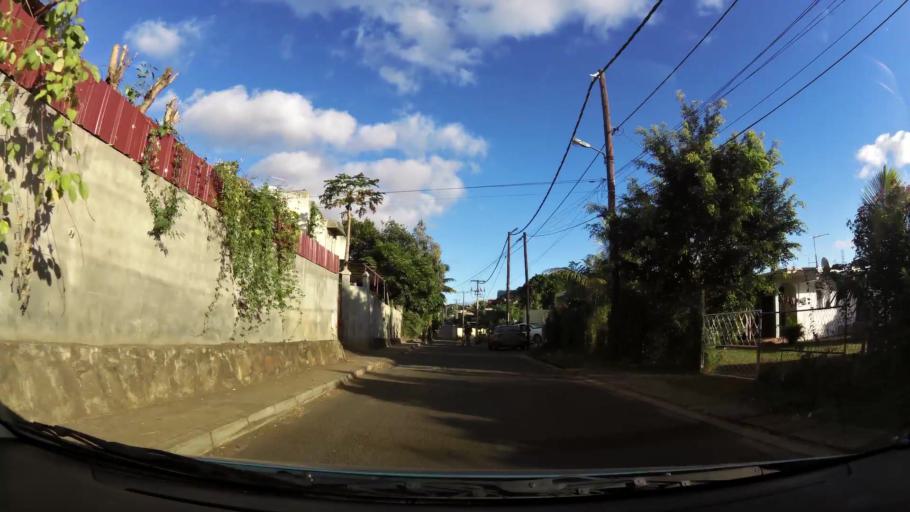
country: MU
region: Black River
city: Petite Riviere
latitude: -20.2167
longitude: 57.4622
